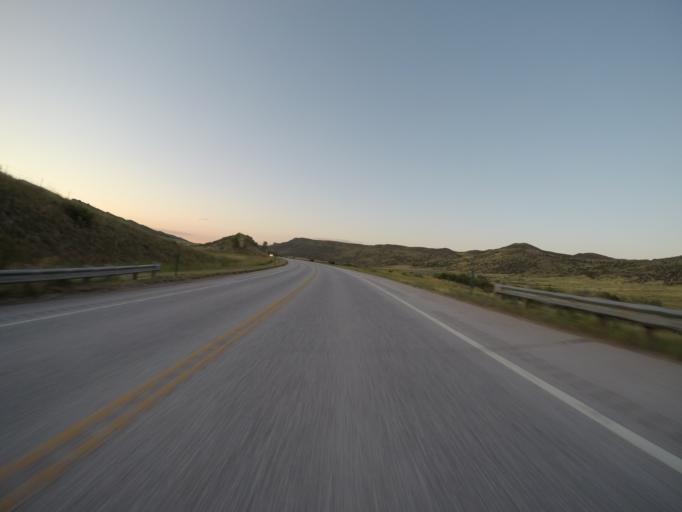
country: US
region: Colorado
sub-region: Larimer County
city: Laporte
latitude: 40.6775
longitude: -105.1793
